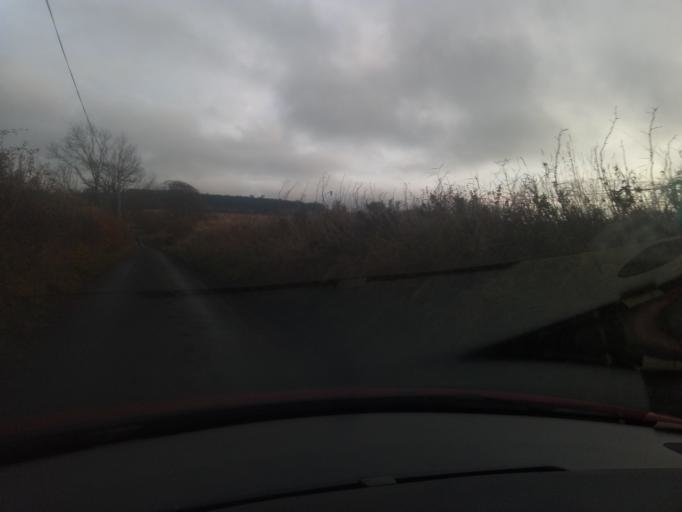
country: GB
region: Scotland
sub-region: The Scottish Borders
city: Jedburgh
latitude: 55.4880
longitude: -2.6156
